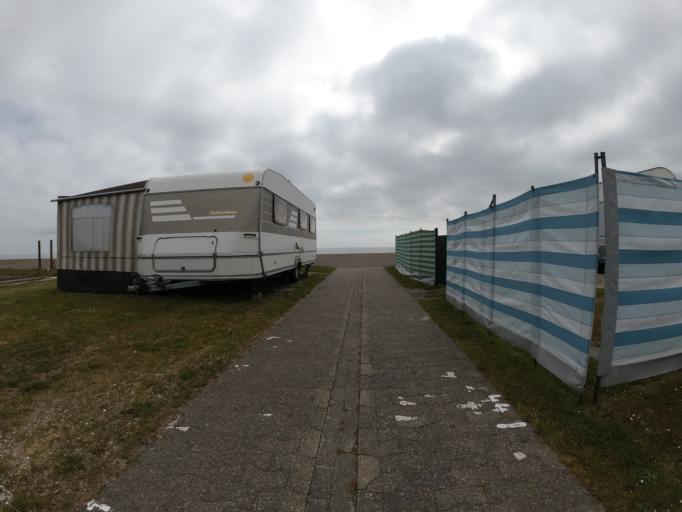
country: DE
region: Lower Saxony
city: Schillig
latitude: 53.6977
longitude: 8.0289
